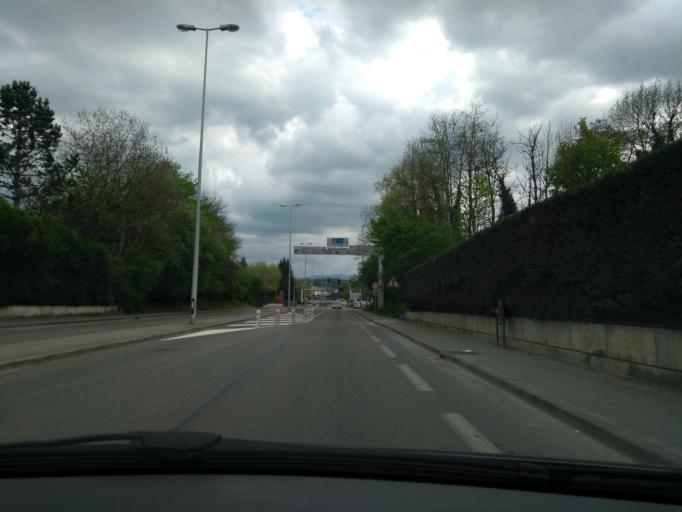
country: FR
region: Rhone-Alpes
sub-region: Departement de la Haute-Savoie
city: Rumilly
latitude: 45.8692
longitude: 5.9382
